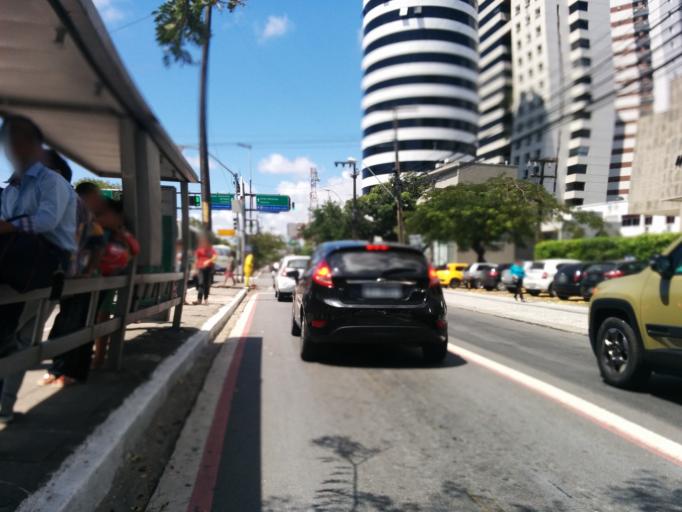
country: BR
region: Pernambuco
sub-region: Recife
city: Recife
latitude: -8.0483
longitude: -34.8930
